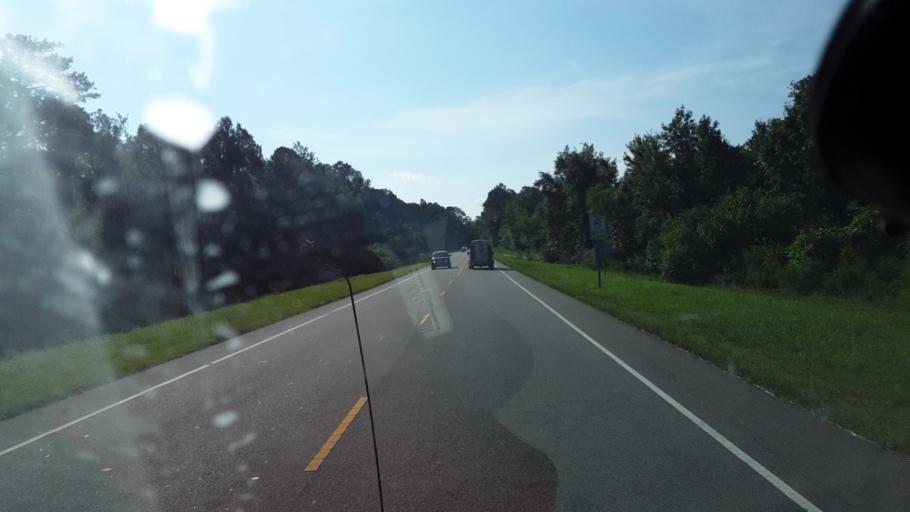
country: US
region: North Carolina
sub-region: Brunswick County
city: Belville
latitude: 34.2291
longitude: -77.9894
